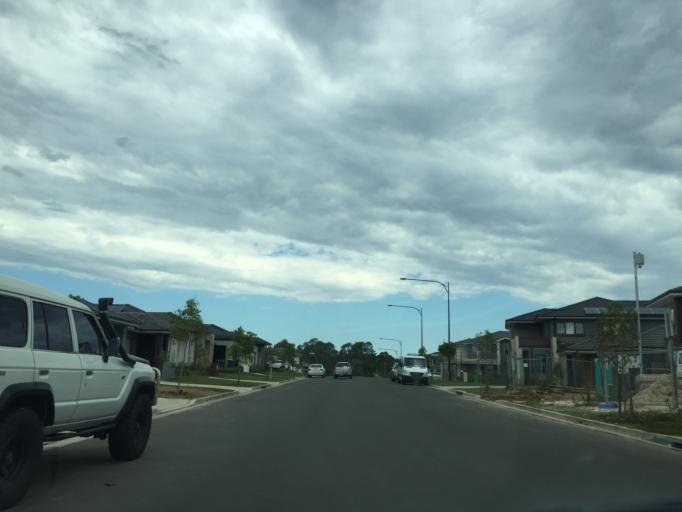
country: AU
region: New South Wales
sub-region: Blacktown
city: Doonside
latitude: -33.7701
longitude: 150.8713
